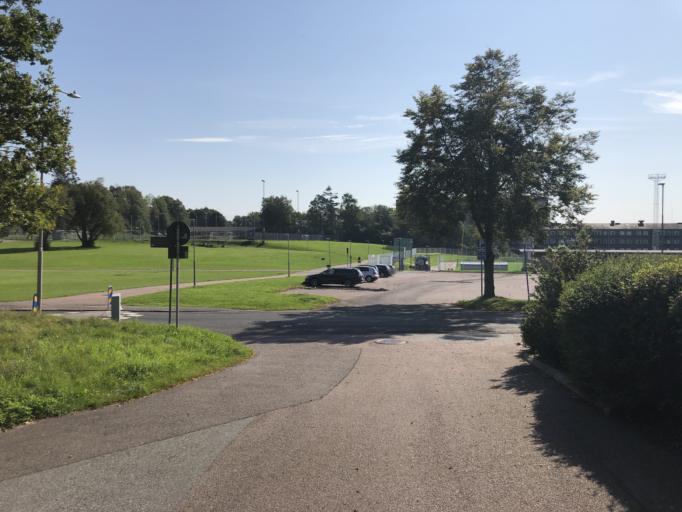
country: SE
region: Vaestra Goetaland
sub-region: Goteborg
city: Goeteborg
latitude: 57.7456
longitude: 11.9636
